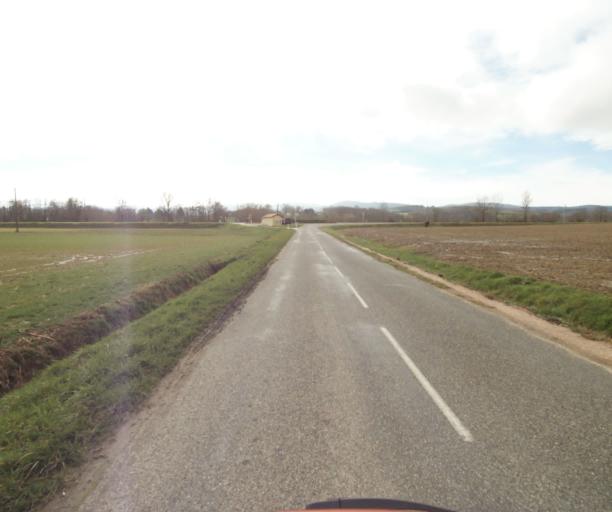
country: FR
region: Midi-Pyrenees
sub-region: Departement de l'Ariege
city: Pamiers
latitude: 43.1092
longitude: 1.5474
